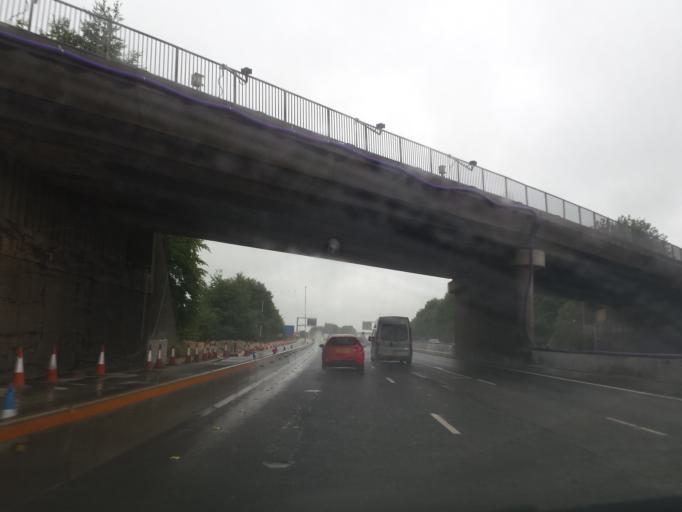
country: GB
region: England
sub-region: Derbyshire
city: Tibshelf
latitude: 53.1359
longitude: -1.3302
